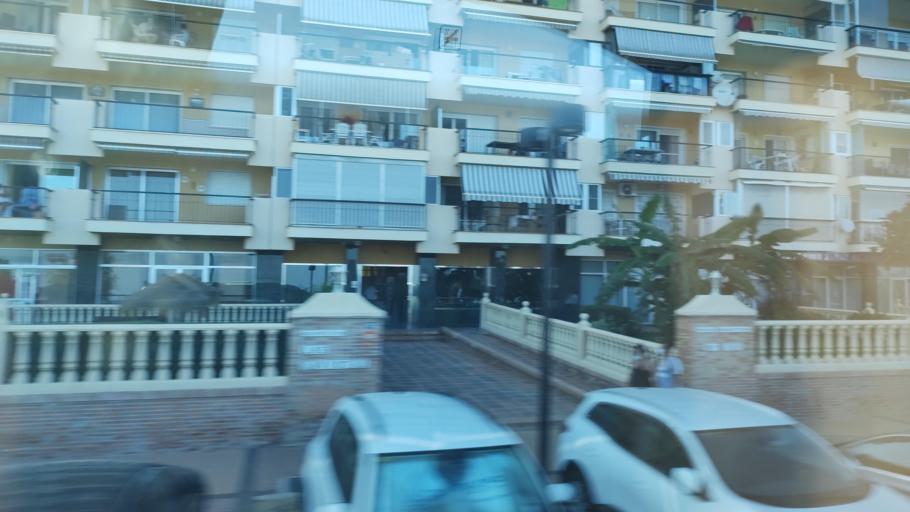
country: ES
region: Andalusia
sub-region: Provincia de Malaga
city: Fuengirola
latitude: 36.5608
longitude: -4.6069
